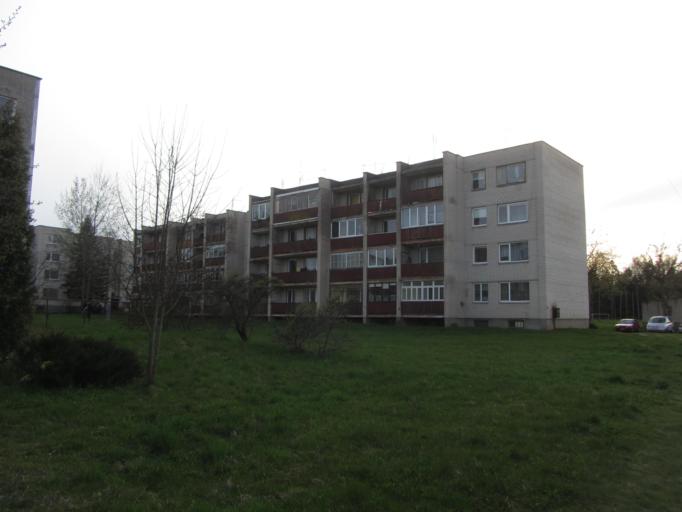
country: LT
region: Utenos apskritis
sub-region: Utena
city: Utena
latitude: 55.7391
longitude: 25.8303
